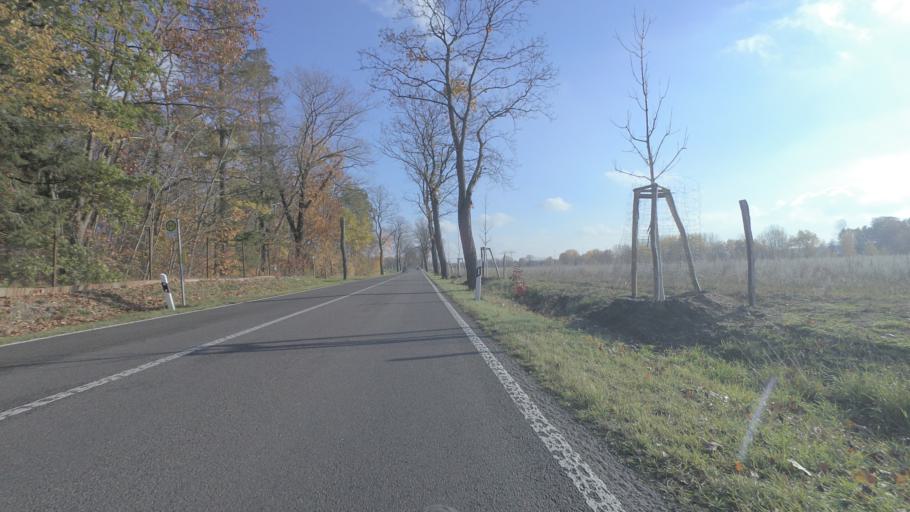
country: DE
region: Brandenburg
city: Ludwigsfelde
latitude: 52.2496
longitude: 13.2840
